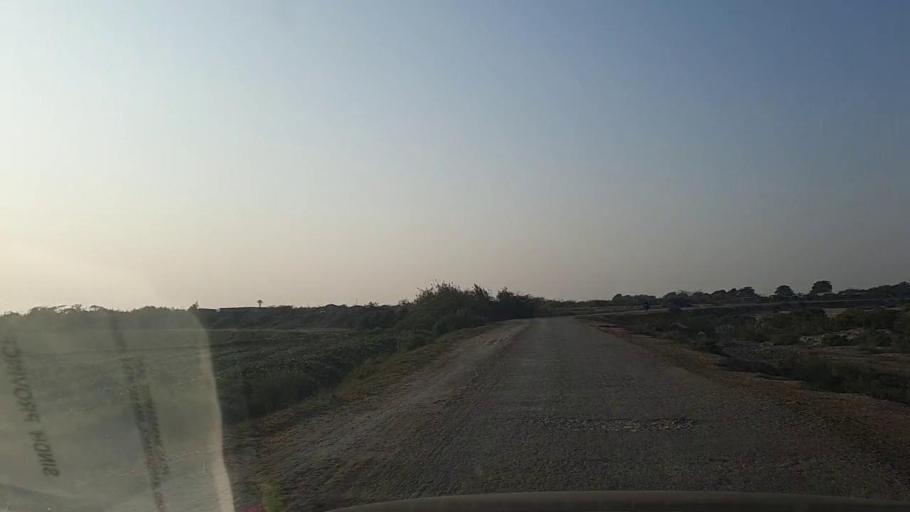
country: PK
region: Sindh
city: Keti Bandar
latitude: 24.2886
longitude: 67.5846
